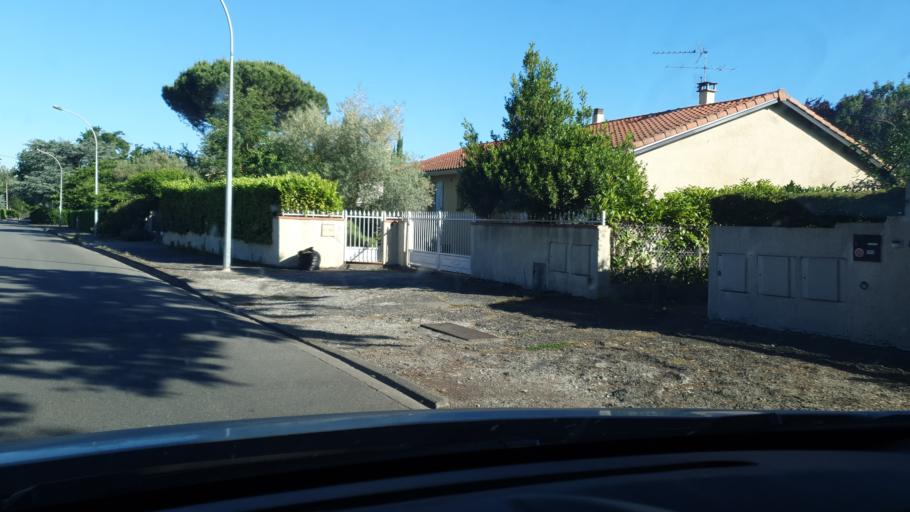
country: FR
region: Midi-Pyrenees
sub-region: Departement de la Haute-Garonne
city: Saint-Orens-de-Gameville
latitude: 43.5581
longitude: 1.5168
